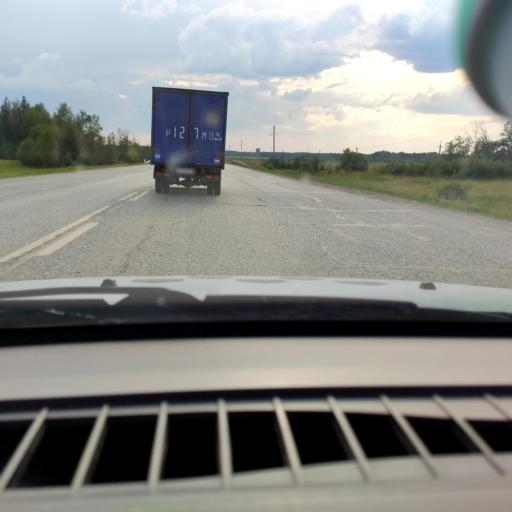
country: RU
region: Udmurtiya
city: Debesy
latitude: 57.6311
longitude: 53.7622
